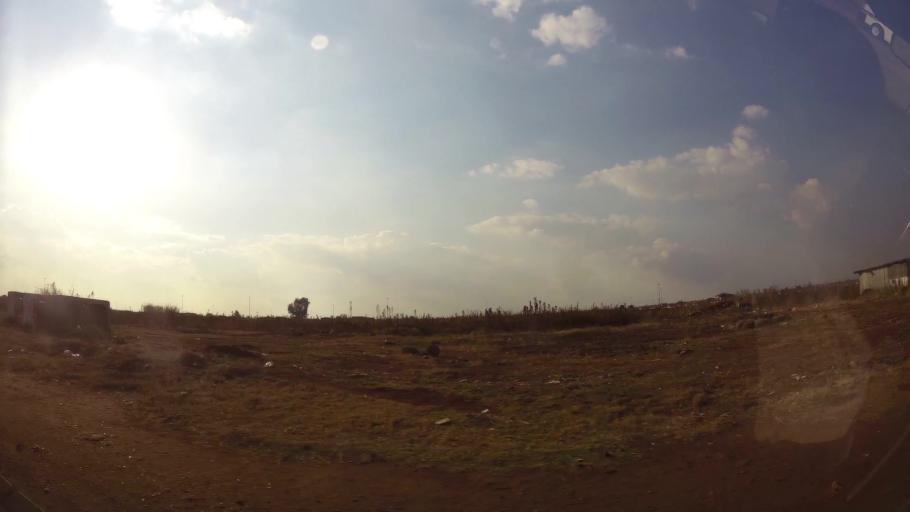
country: ZA
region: Gauteng
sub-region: Ekurhuleni Metropolitan Municipality
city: Germiston
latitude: -26.3696
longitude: 28.1937
